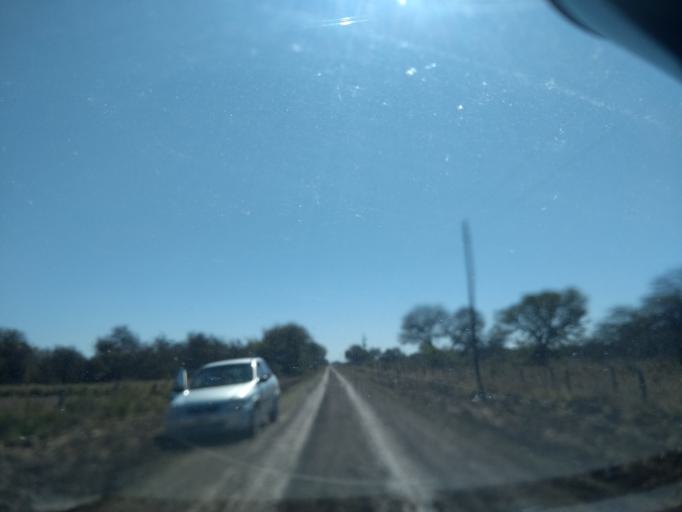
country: AR
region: Chaco
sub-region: Departamento de Quitilipi
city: Quitilipi
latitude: -26.7459
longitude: -60.2384
